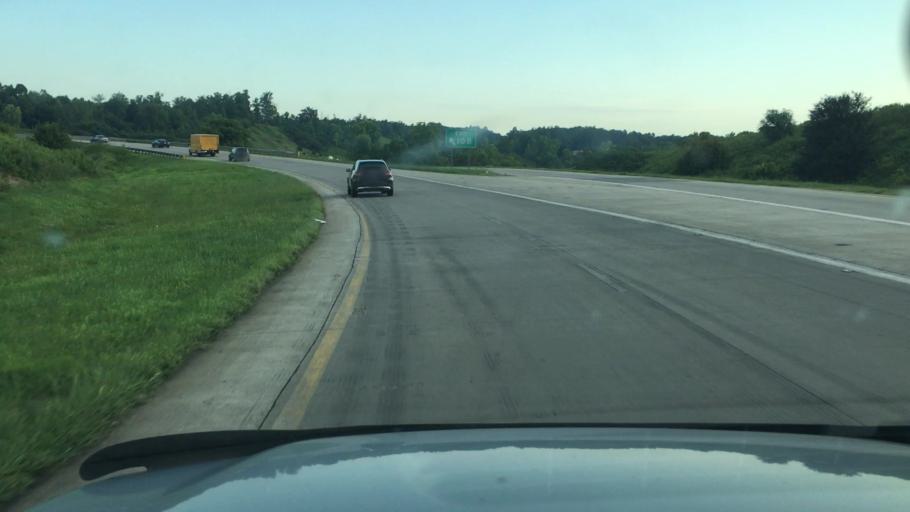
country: US
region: North Carolina
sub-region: Gaston County
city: Mount Holly
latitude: 35.2498
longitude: -80.9673
